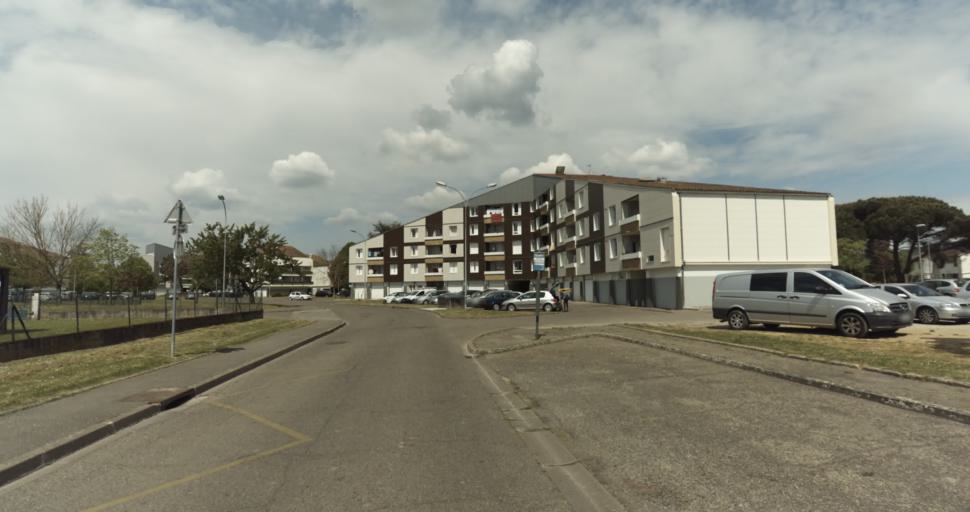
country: FR
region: Aquitaine
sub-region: Departement du Lot-et-Garonne
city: Agen
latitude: 44.1890
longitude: 0.6349
